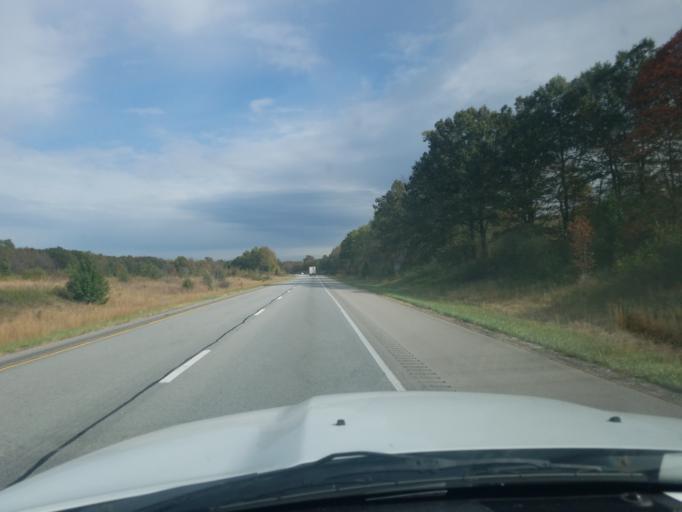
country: US
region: Indiana
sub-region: Warrick County
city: Chandler
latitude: 38.1833
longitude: -87.3779
